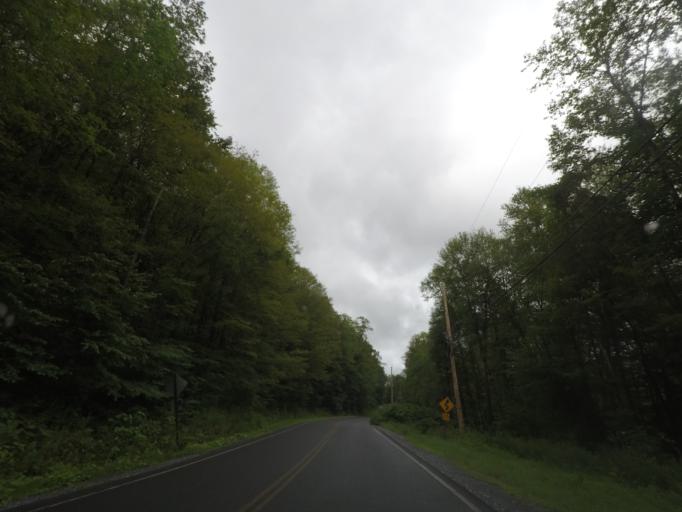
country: US
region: New York
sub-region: Rensselaer County
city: Averill Park
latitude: 42.6892
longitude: -73.3883
